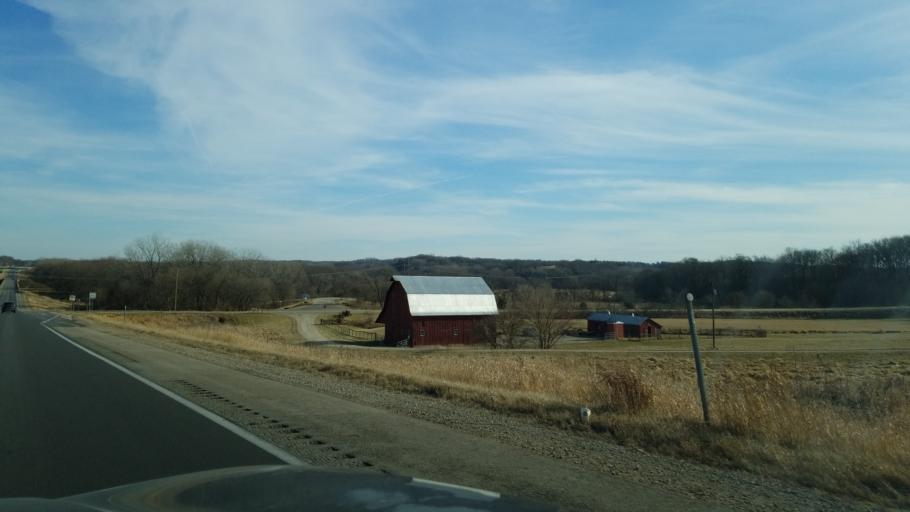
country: US
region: Iowa
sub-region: Linn County
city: Ely
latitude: 41.9255
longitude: -91.5578
